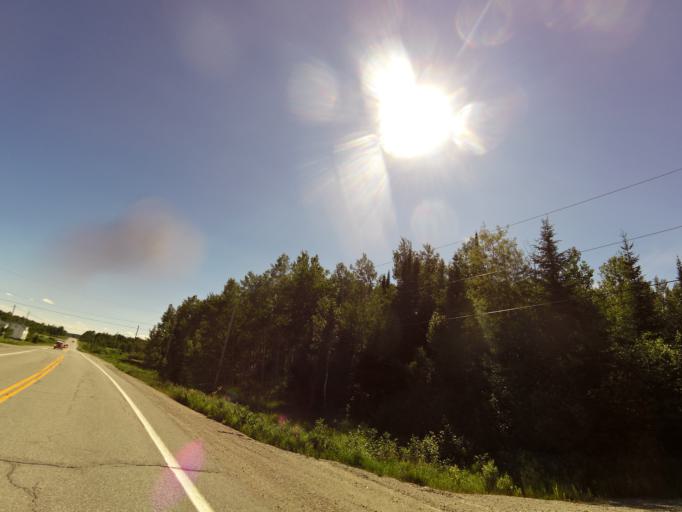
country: CA
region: Quebec
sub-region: Abitibi-Temiscamingue
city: Senneterre
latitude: 48.2245
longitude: -77.3457
